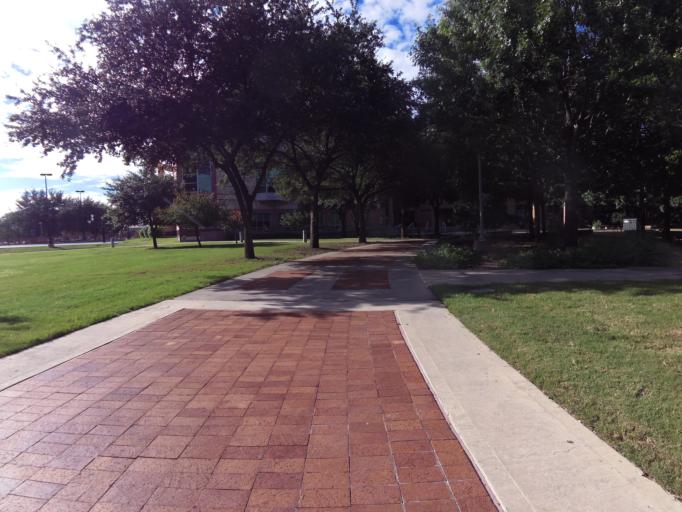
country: US
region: Texas
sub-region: Bexar County
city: San Antonio
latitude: 29.4234
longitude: -98.5030
